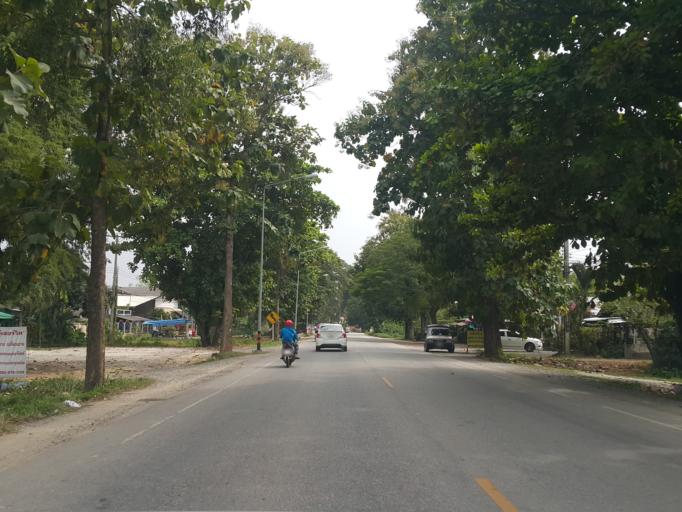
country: TH
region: Chiang Mai
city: Mae Taeng
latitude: 18.9832
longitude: 98.9785
